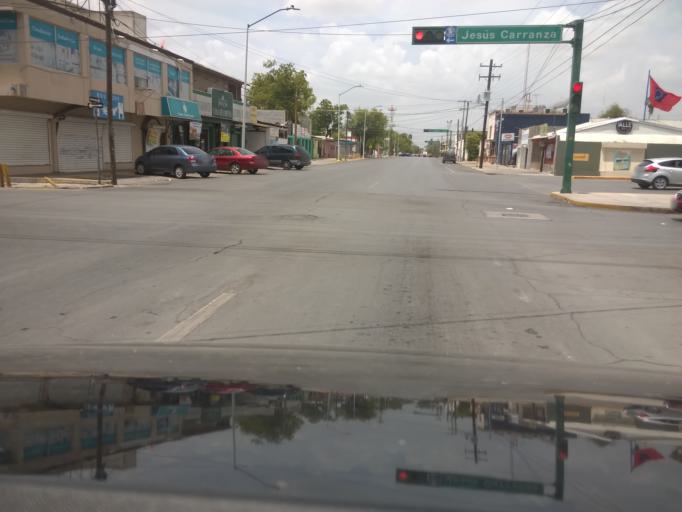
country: MX
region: Tamaulipas
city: Nuevo Laredo
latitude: 27.4867
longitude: -99.5017
